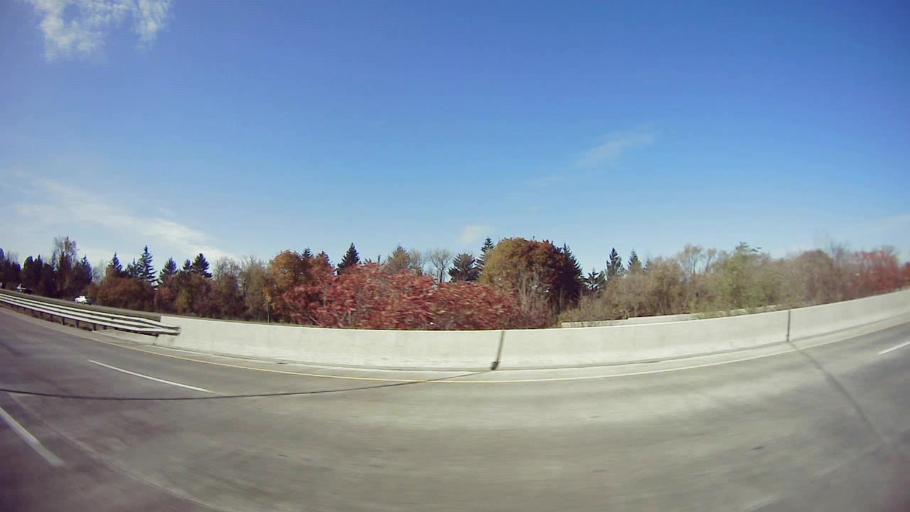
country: US
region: Michigan
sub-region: Wayne County
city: Canton
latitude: 42.3058
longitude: -83.4423
